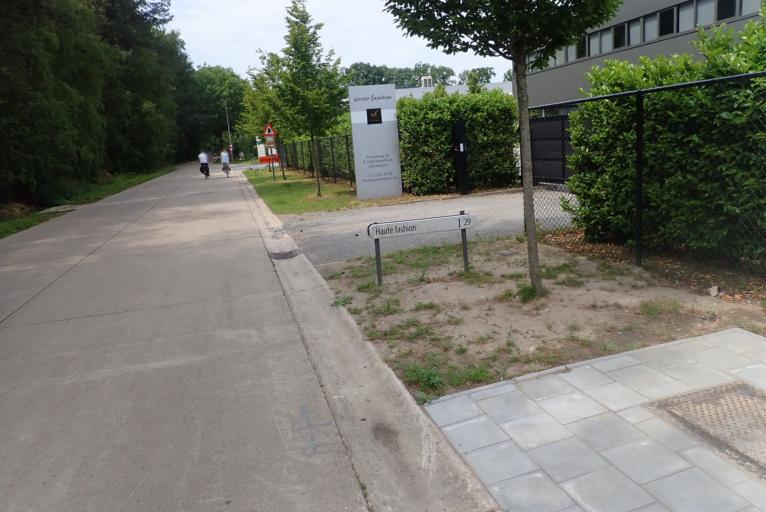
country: BE
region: Flanders
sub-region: Provincie Antwerpen
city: Kalmthout
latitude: 51.3655
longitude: 4.5002
